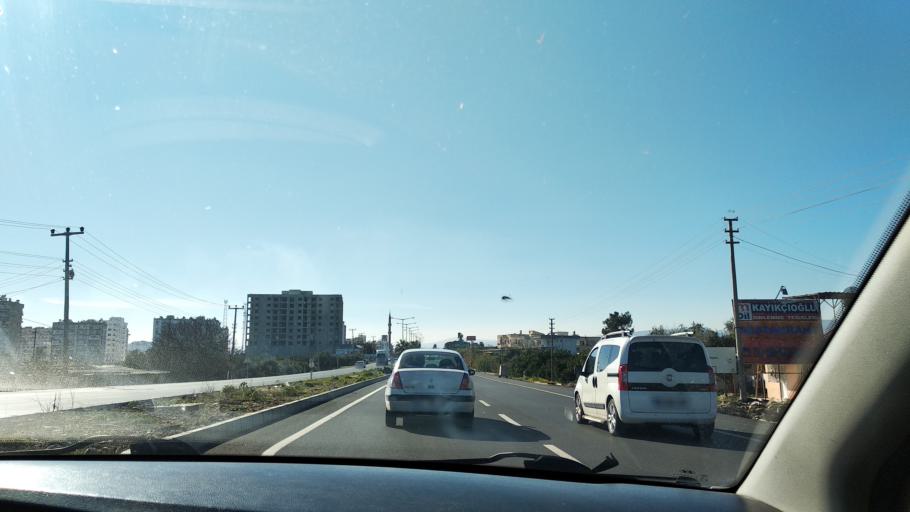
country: TR
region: Mersin
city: Tomuk
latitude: 36.6545
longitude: 34.3879
